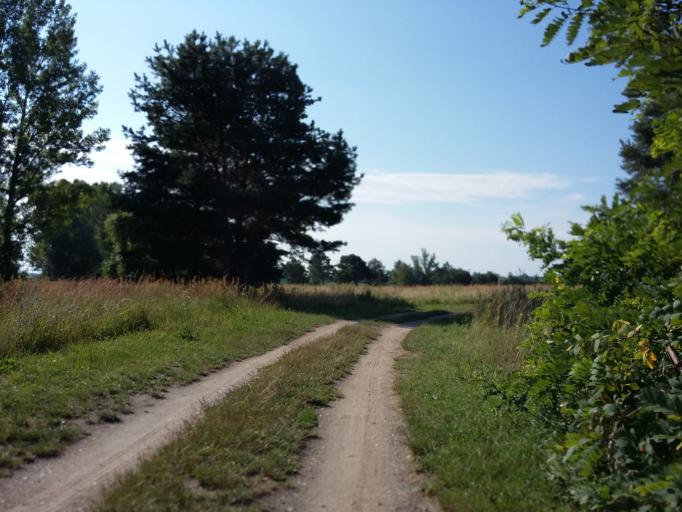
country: AT
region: Lower Austria
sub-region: Politischer Bezirk Ganserndorf
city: Drosing
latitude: 48.4943
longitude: 16.9611
